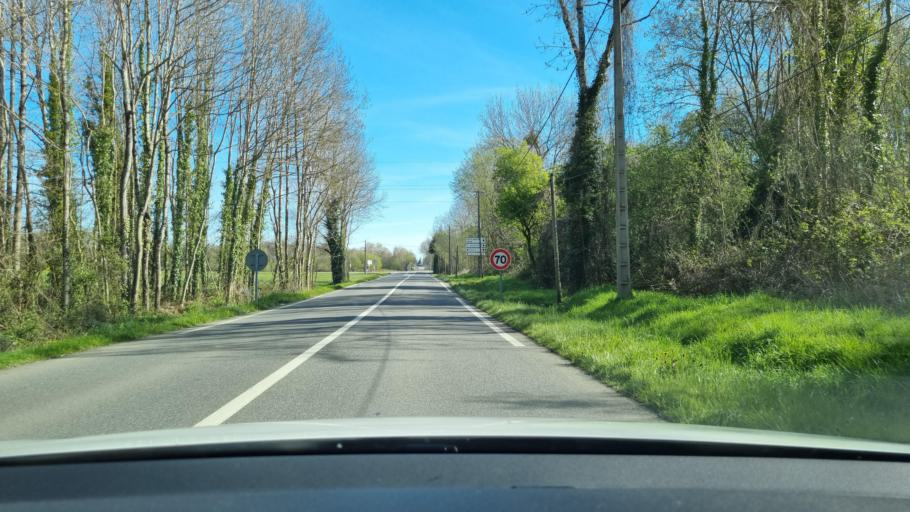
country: FR
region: Midi-Pyrenees
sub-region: Departement des Hautes-Pyrenees
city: Lannemezan
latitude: 43.1053
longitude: 0.4017
